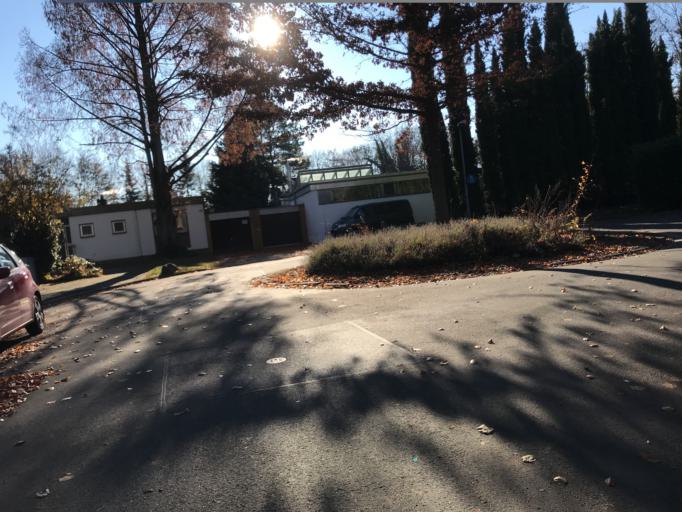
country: DE
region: Rheinland-Pfalz
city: Mainz
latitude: 49.9777
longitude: 8.2534
